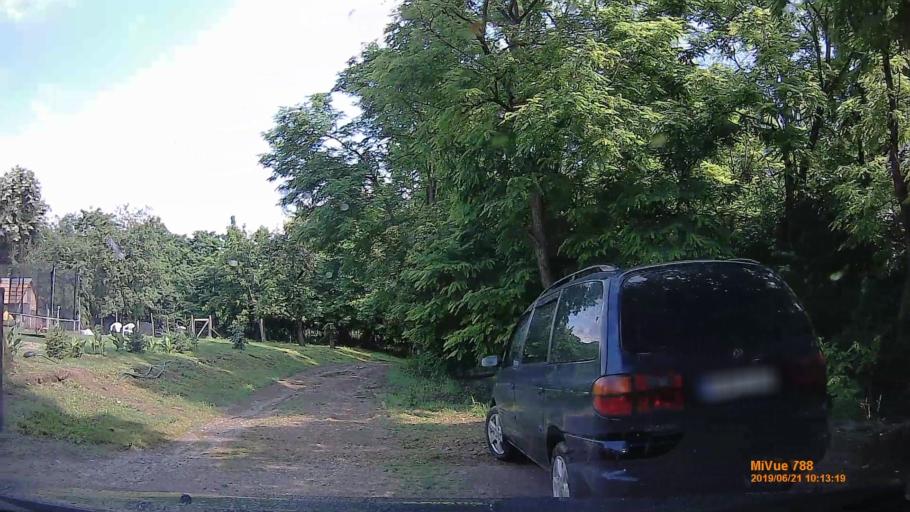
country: HU
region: Baranya
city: Buekkoesd
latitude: 46.1958
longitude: 17.9566
